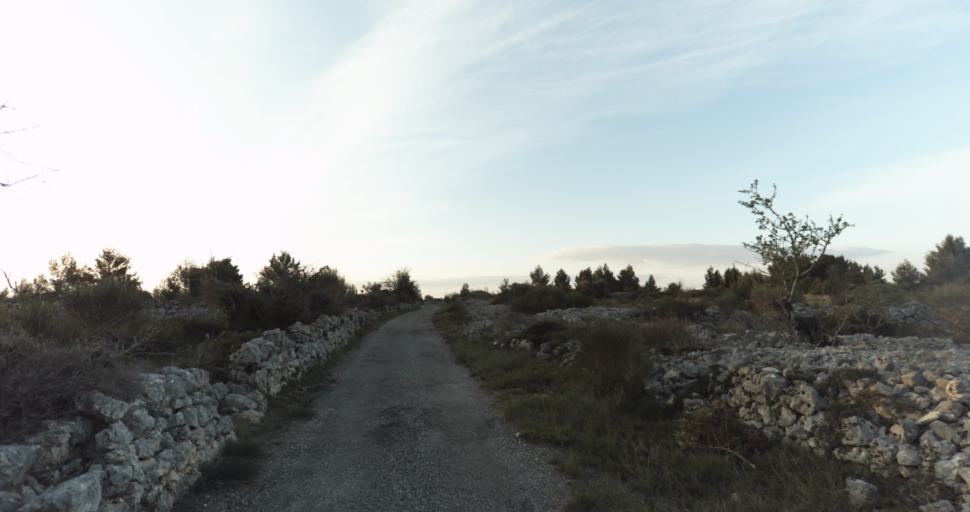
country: FR
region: Languedoc-Roussillon
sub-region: Departement de l'Aude
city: Leucate
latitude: 42.9248
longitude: 3.0225
